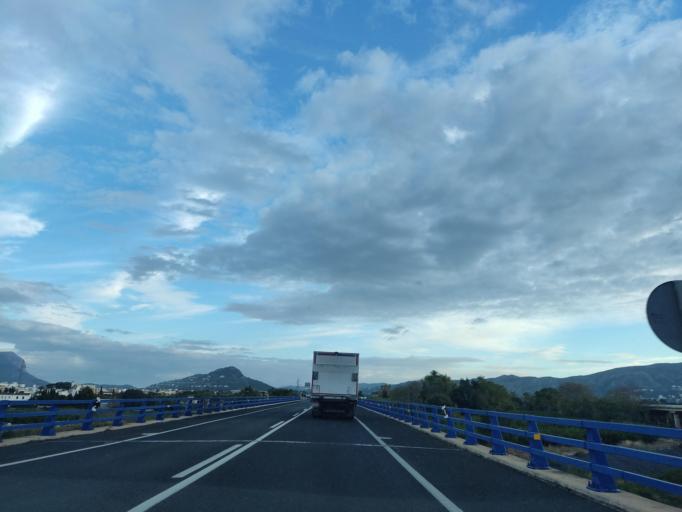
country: ES
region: Valencia
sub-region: Provincia de Alicante
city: Beniarbeig
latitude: 38.8285
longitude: 0.0062
